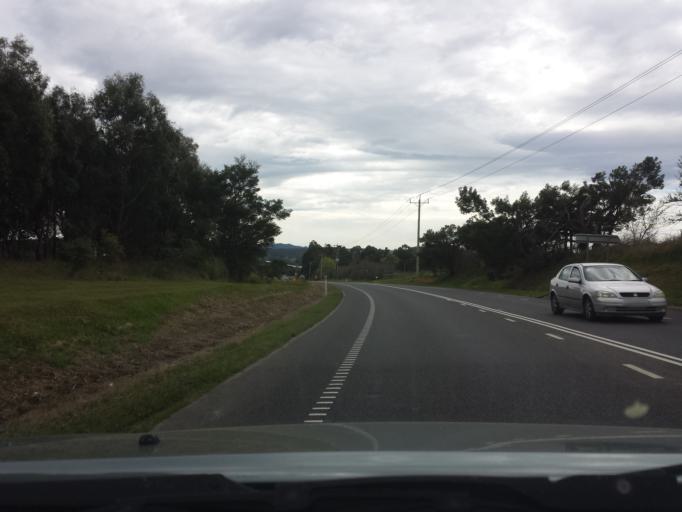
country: AU
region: Victoria
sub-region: Casey
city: Narre Warren North
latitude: -37.9761
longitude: 145.3149
